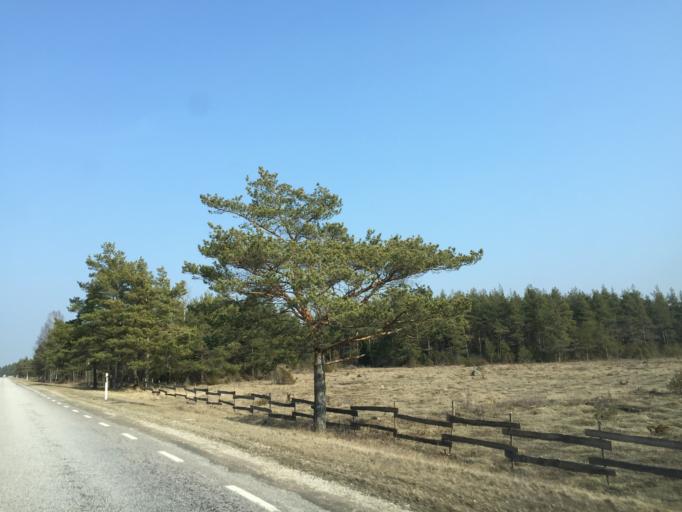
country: EE
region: Saare
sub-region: Kuressaare linn
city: Kuressaare
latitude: 58.3755
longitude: 22.7320
